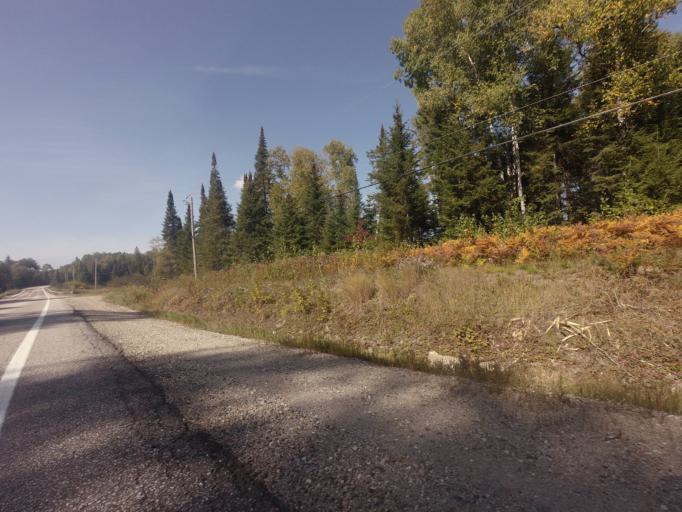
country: CA
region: Quebec
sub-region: Outaouais
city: Maniwaki
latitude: 46.5525
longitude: -75.7681
